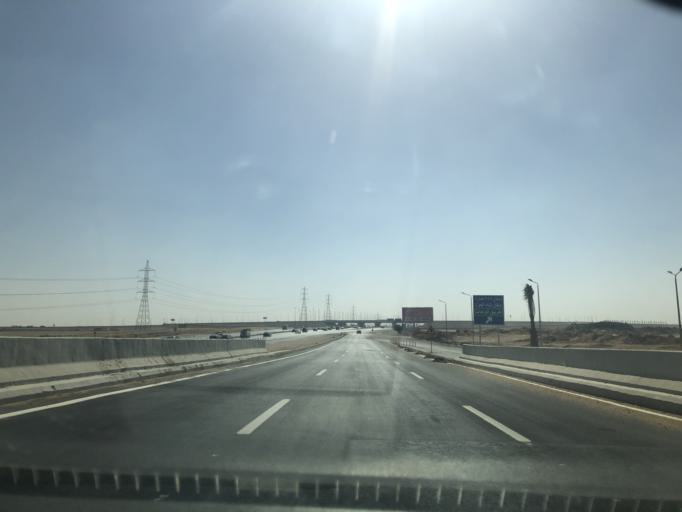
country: EG
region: Al Jizah
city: Madinat Sittah Uktubar
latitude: 29.8737
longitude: 31.0742
